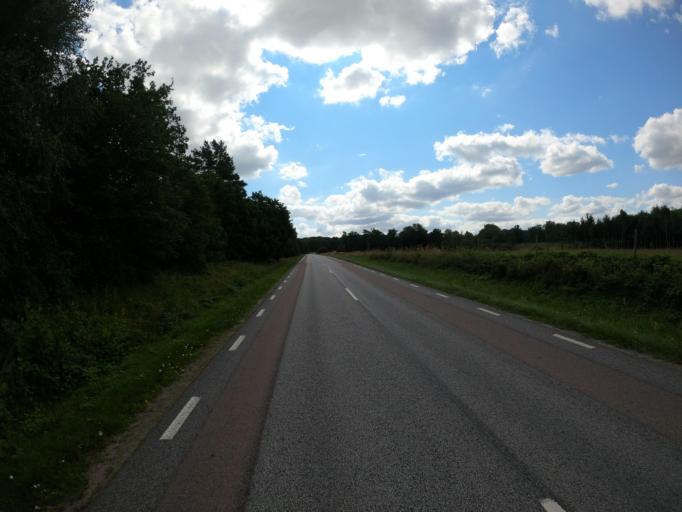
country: SE
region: Skane
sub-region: Lunds Kommun
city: Veberod
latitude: 55.6213
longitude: 13.4928
